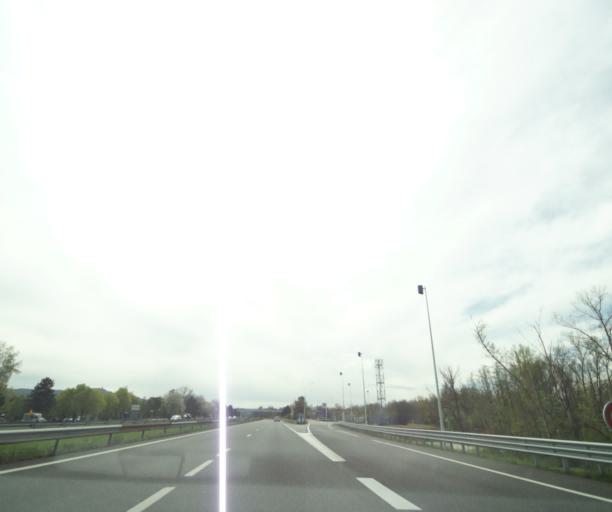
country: FR
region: Rhone-Alpes
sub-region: Departement du Rhone
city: Les Cheres
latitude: 45.9064
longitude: 4.7282
